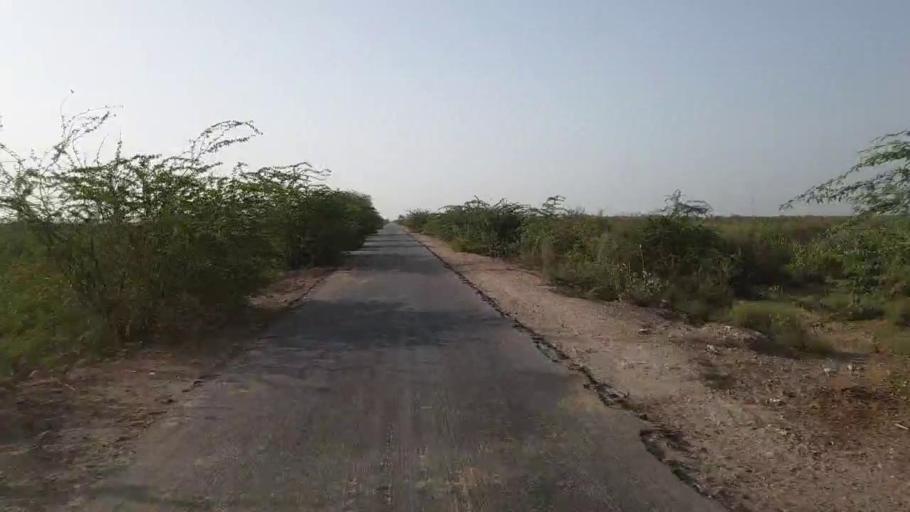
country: PK
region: Sindh
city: Jam Sahib
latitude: 26.4437
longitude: 68.8653
